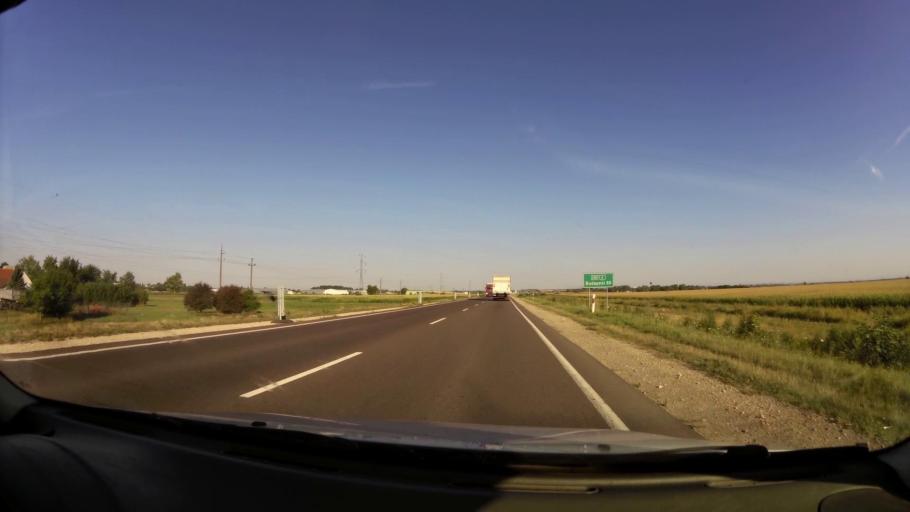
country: HU
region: Pest
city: Cegled
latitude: 47.1986
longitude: 19.8006
